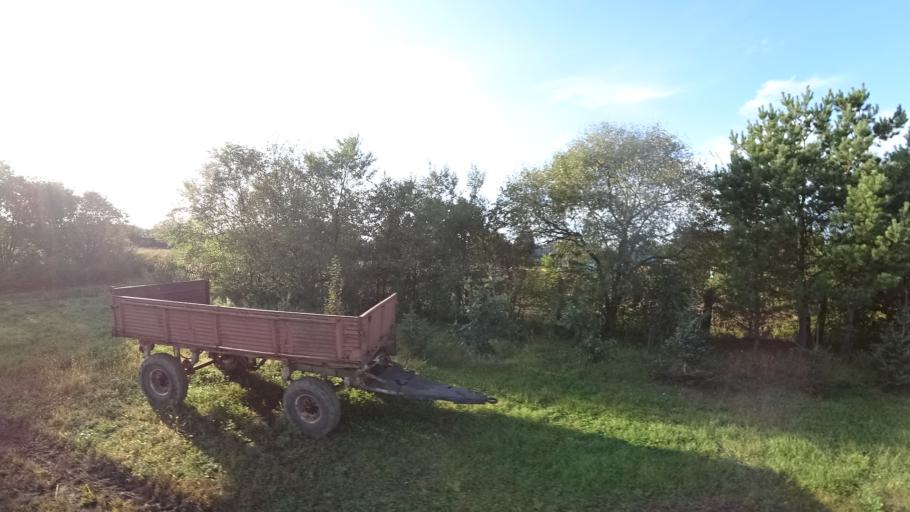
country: RU
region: Amur
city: Arkhara
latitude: 49.3605
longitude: 130.1272
